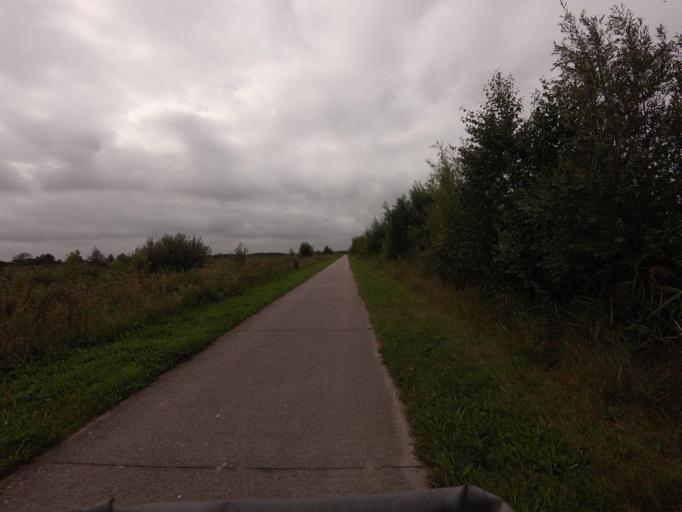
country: NL
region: Overijssel
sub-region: Gemeente Steenwijkerland
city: Giethoorn
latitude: 52.7130
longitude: 6.0670
